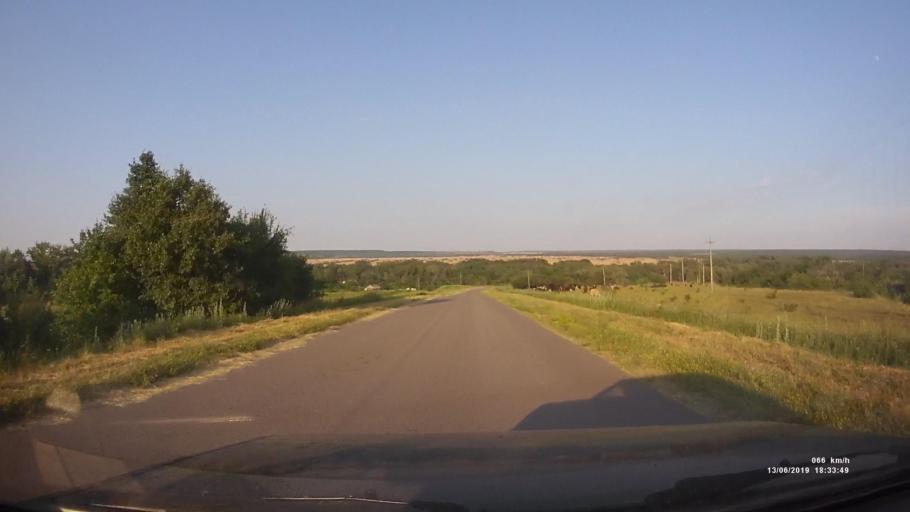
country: RU
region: Rostov
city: Kazanskaya
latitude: 49.8704
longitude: 41.3883
